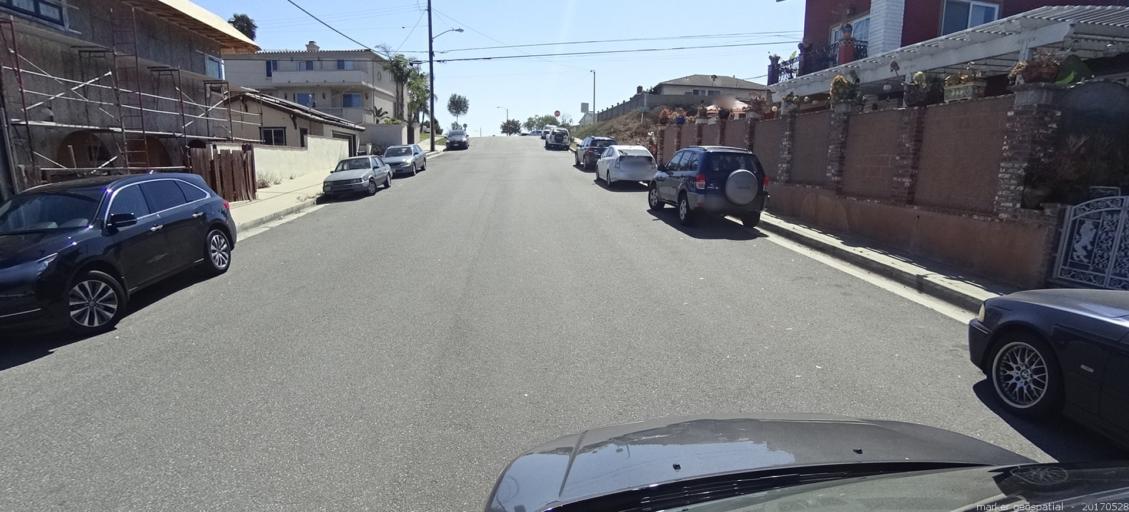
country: US
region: California
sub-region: Los Angeles County
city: Redondo Beach
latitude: 33.8458
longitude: -118.3771
